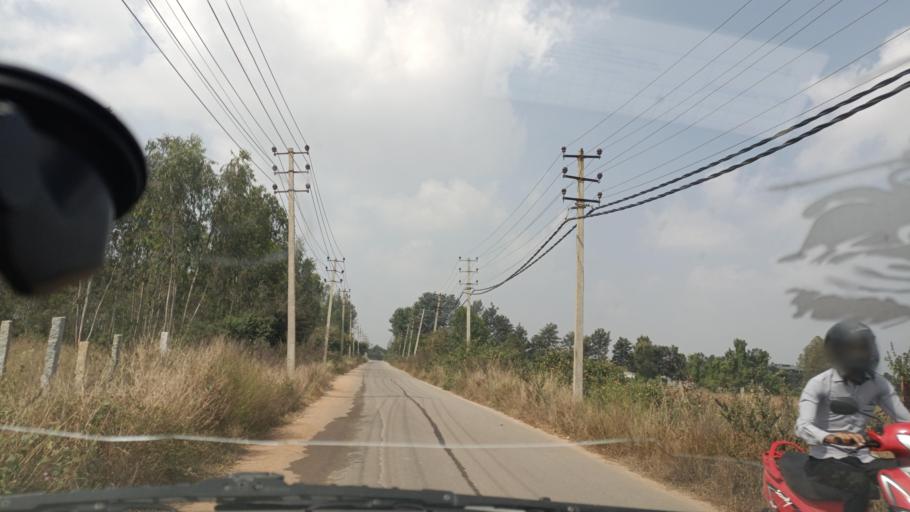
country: IN
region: Karnataka
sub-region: Bangalore Urban
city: Yelahanka
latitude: 13.1526
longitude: 77.6308
